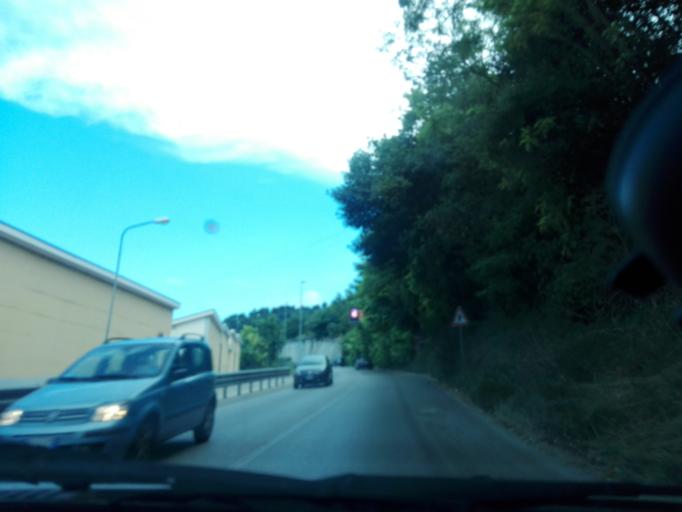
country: IT
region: Abruzzo
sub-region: Provincia di Pescara
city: Montesilvano Marina
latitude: 42.4998
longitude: 14.1407
